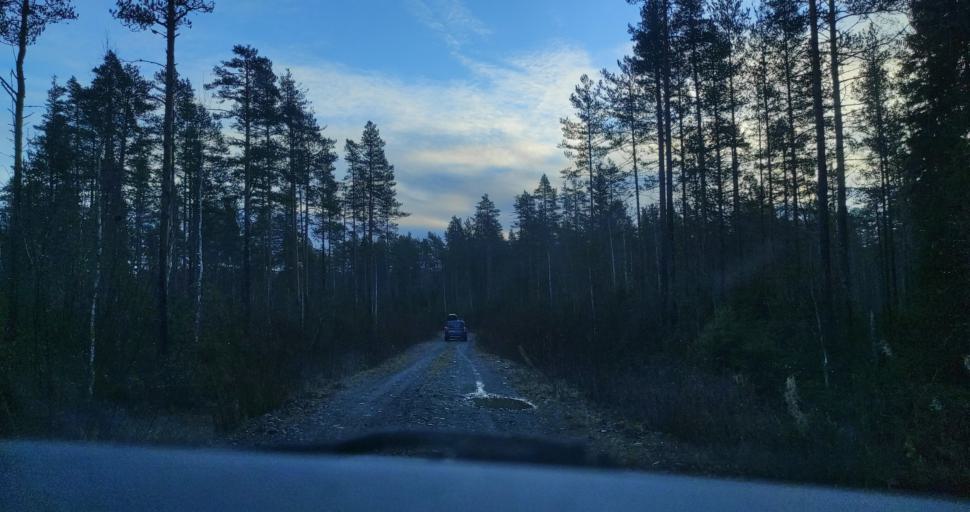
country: RU
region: Republic of Karelia
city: Pitkyaranta
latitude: 61.7345
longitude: 31.3683
